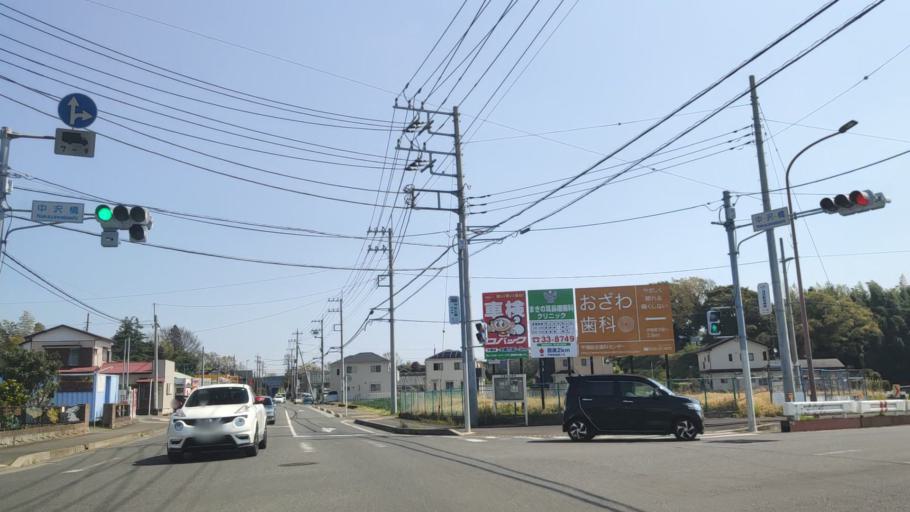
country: JP
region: Kanagawa
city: Oiso
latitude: 35.3421
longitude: 139.2936
